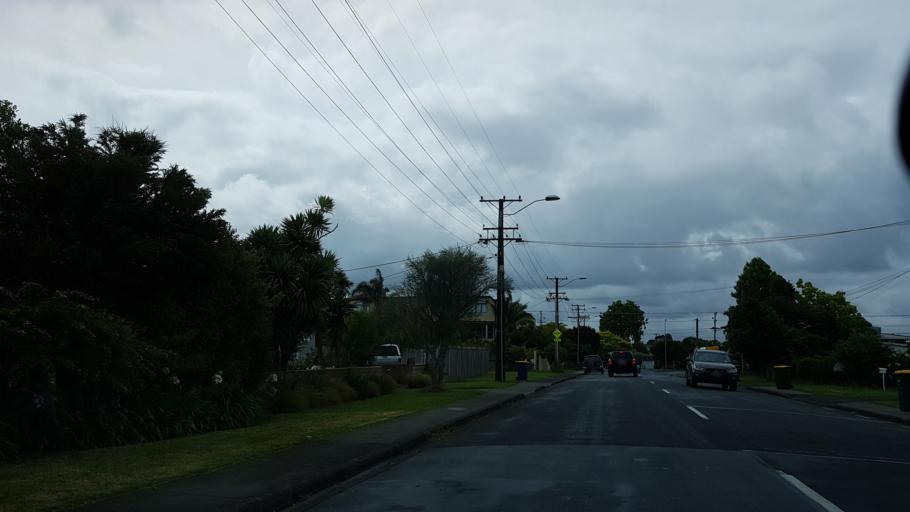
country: NZ
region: Auckland
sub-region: Auckland
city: North Shore
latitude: -36.7937
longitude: 174.7432
